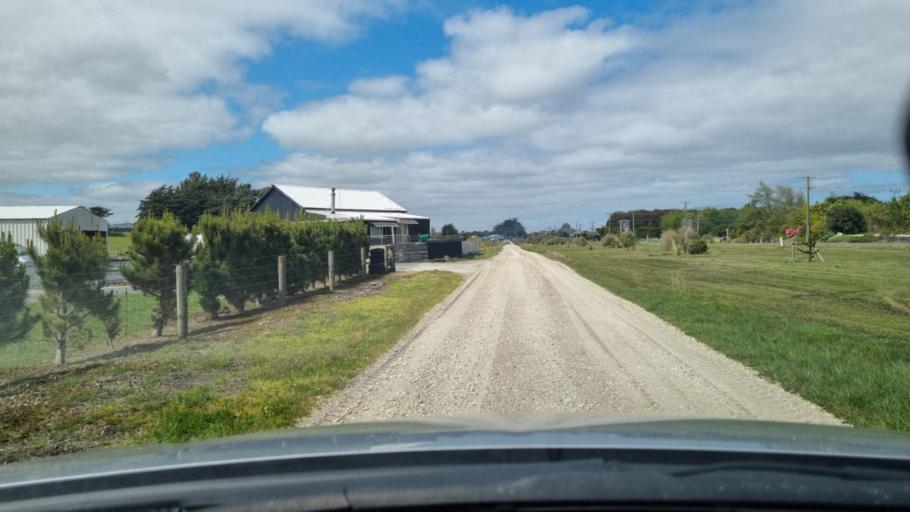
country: NZ
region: Southland
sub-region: Invercargill City
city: Invercargill
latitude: -46.4414
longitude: 168.3921
